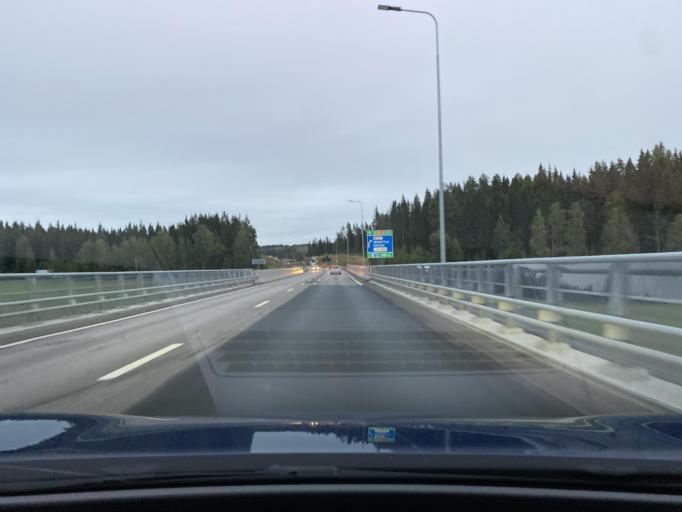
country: FI
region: Paijanne Tavastia
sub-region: Lahti
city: Hollola
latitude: 60.9551
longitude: 25.5658
